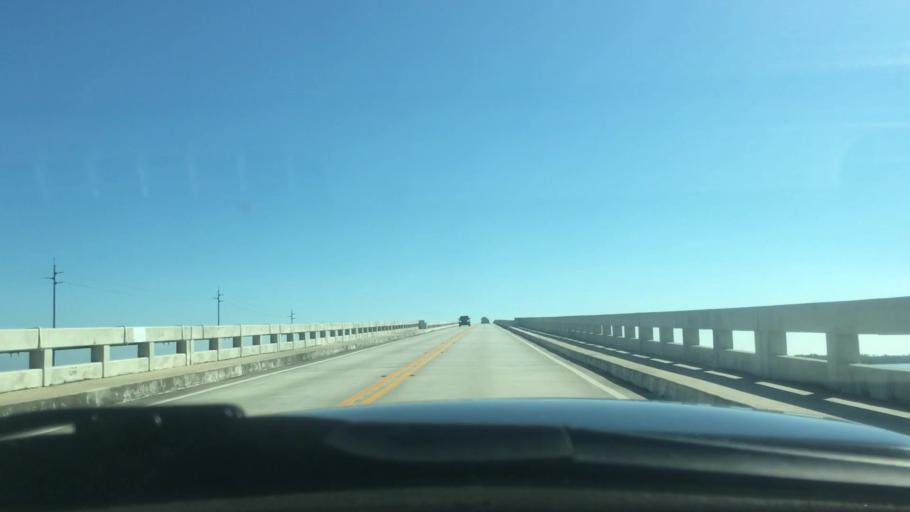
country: US
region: Florida
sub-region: Monroe County
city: North Key Largo
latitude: 25.2887
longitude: -80.3719
